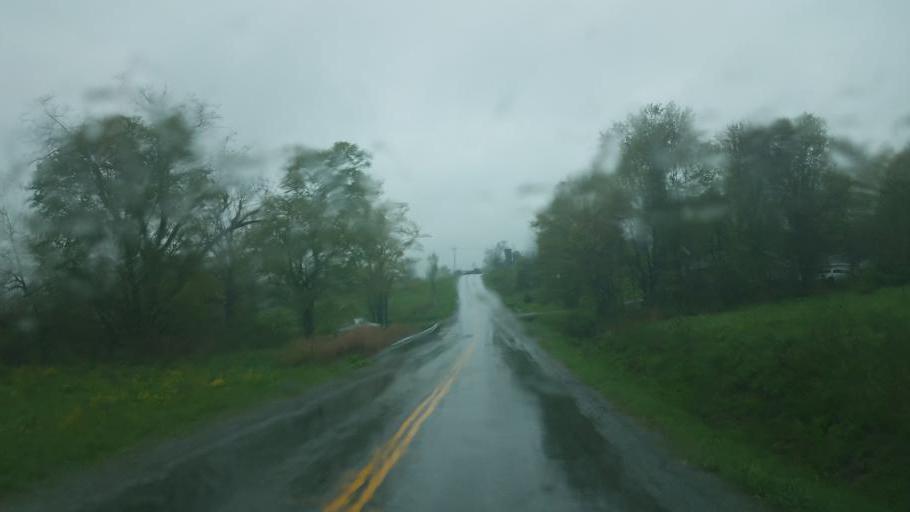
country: US
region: Pennsylvania
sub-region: Tioga County
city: Westfield
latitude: 42.0822
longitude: -77.4881
